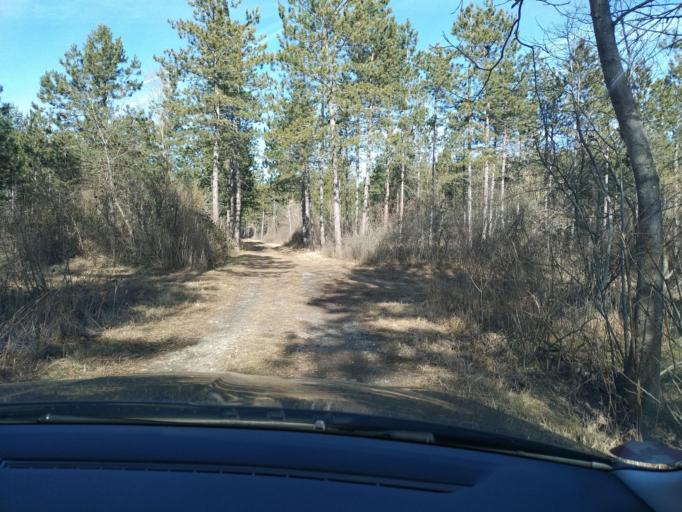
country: AT
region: Lower Austria
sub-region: Politischer Bezirk Neunkirchen
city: Breitenau
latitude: 47.7445
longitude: 16.1652
